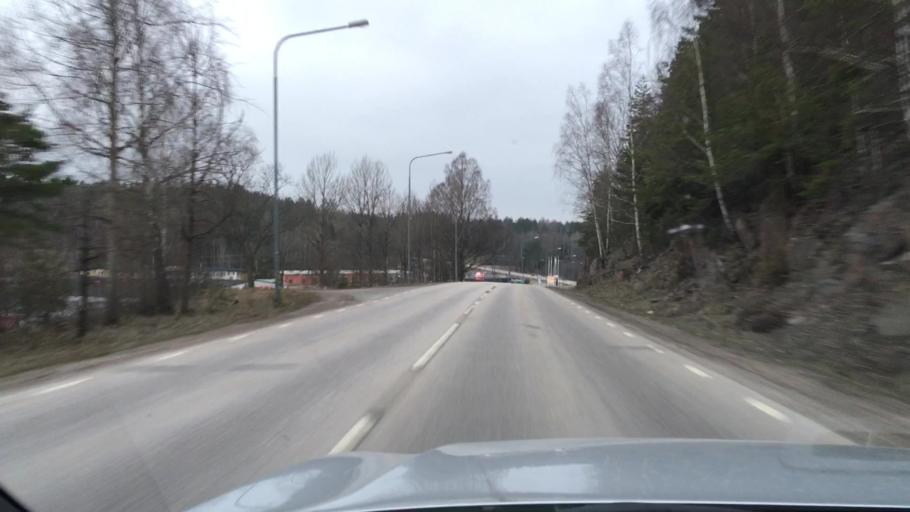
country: SE
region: OEstergoetland
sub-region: Valdemarsviks Kommun
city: Valdemarsvik
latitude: 58.2147
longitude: 16.5813
